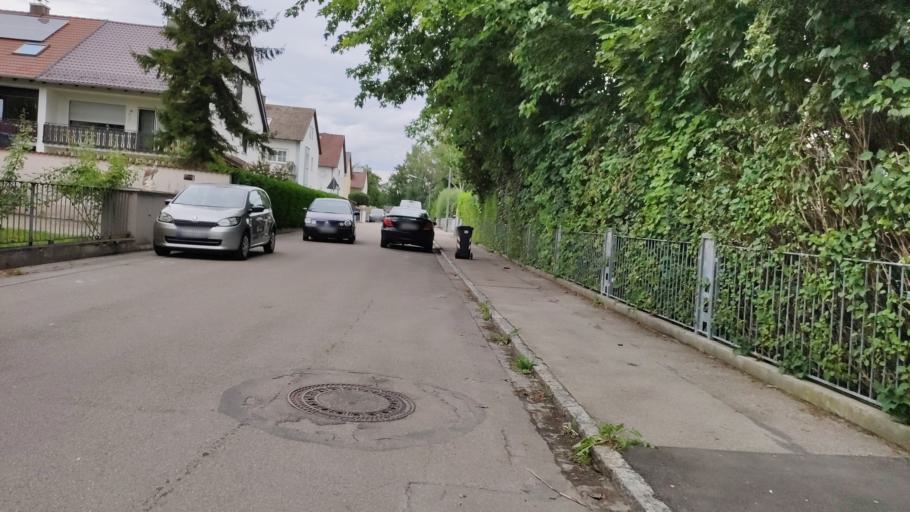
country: DE
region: Bavaria
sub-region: Swabia
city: Konigsbrunn
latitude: 48.2694
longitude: 10.8933
